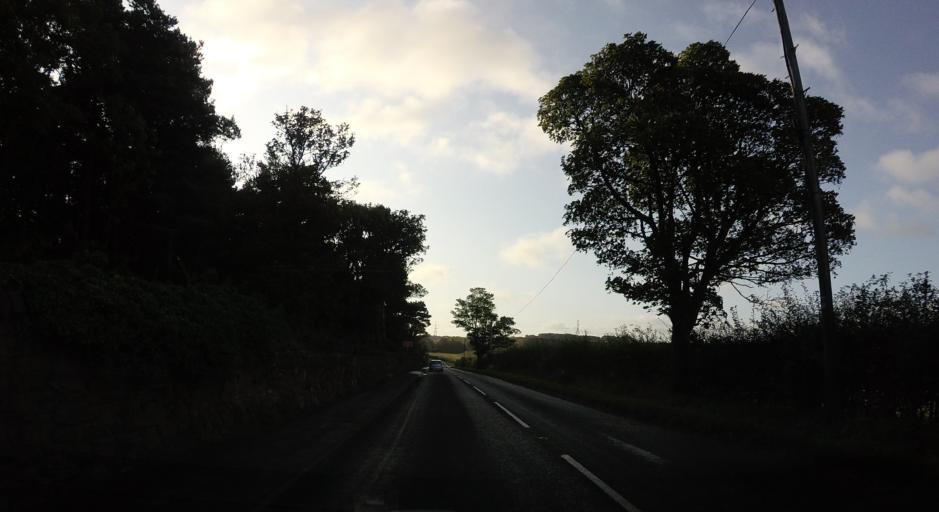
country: GB
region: Scotland
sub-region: East Lothian
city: Musselburgh
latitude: 55.9141
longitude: -3.0255
